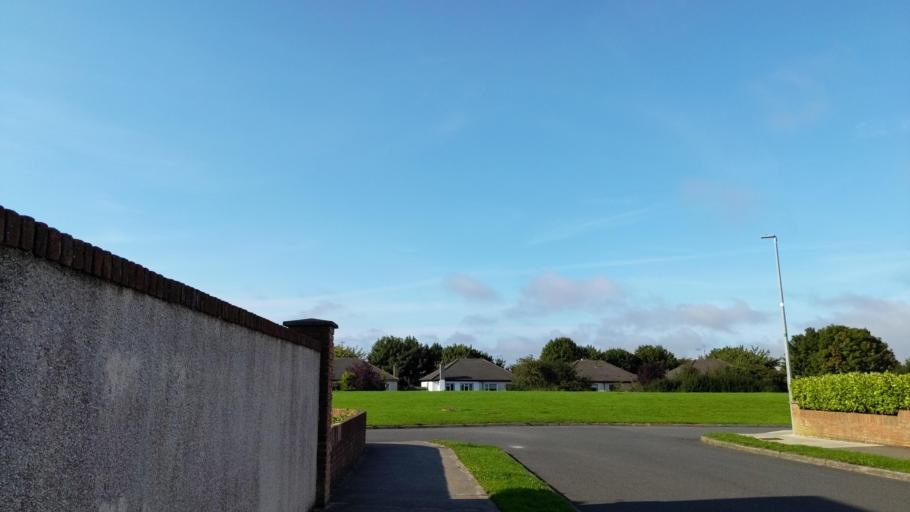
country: IE
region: Leinster
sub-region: Lu
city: Drogheda
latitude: 53.7042
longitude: -6.3514
